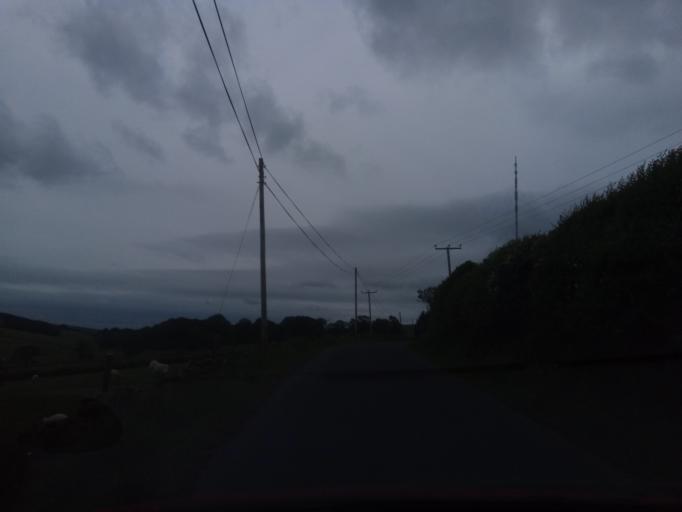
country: GB
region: Scotland
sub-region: The Scottish Borders
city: Selkirk
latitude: 55.5590
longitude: -2.8028
